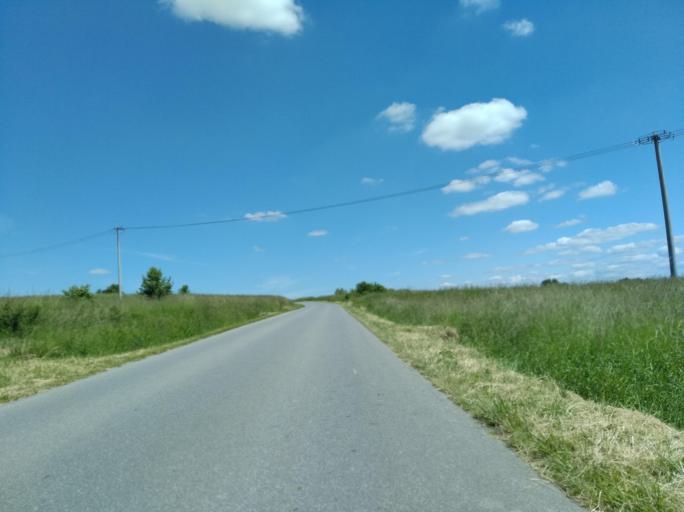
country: PL
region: Subcarpathian Voivodeship
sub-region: Powiat jasielski
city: Osiek Jasielski
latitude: 49.6530
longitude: 21.5291
